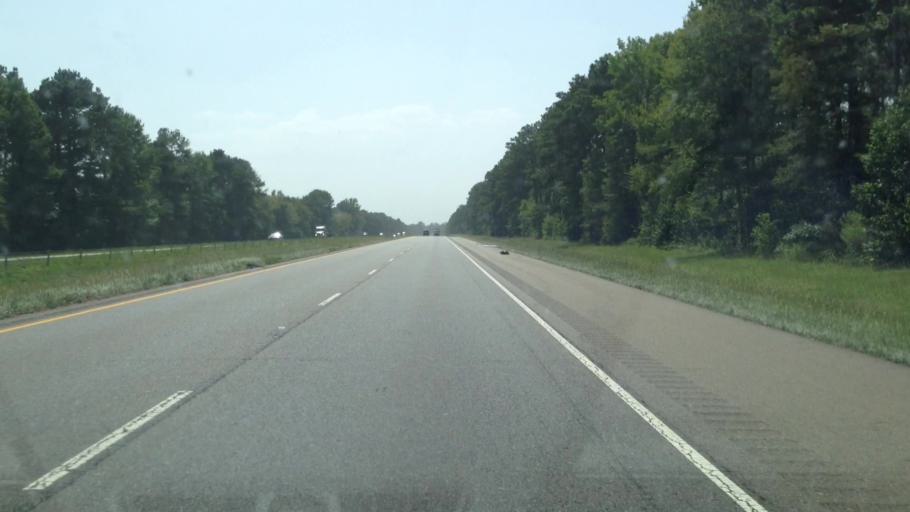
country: US
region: Louisiana
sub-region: Bossier Parish
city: Haughton
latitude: 32.5773
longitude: -93.4529
